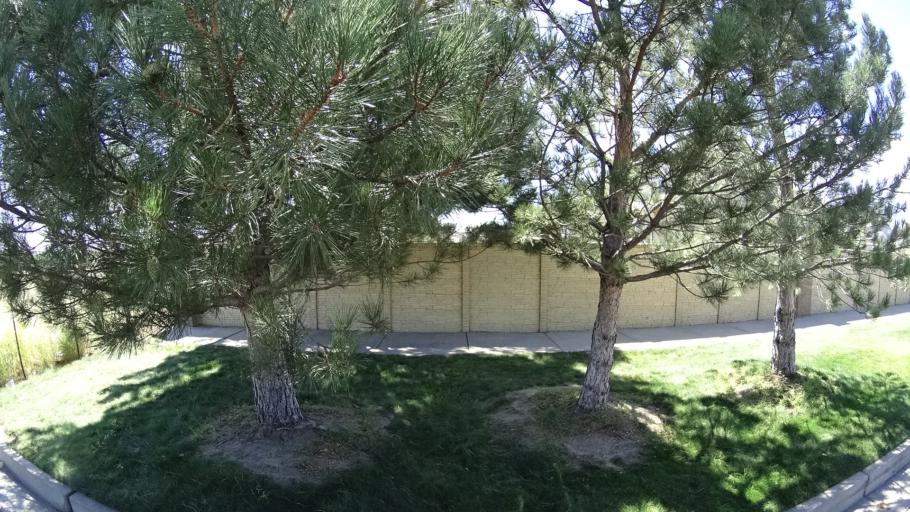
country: US
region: Colorado
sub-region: El Paso County
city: Security-Widefield
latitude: 38.7835
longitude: -104.7261
